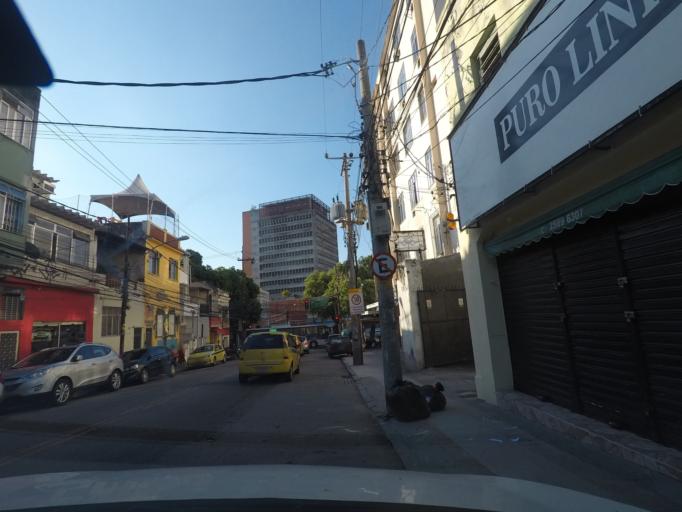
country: BR
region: Rio de Janeiro
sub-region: Rio De Janeiro
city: Rio de Janeiro
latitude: -22.9005
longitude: -43.2229
